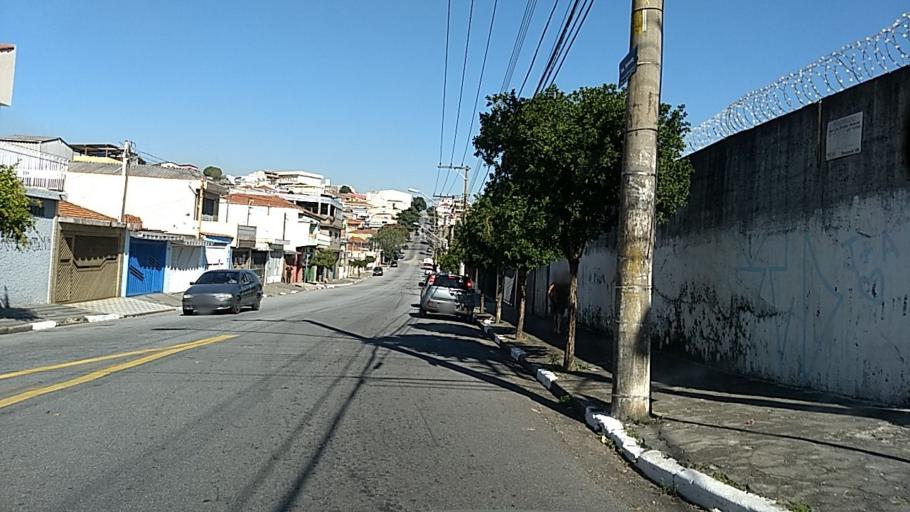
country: BR
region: Sao Paulo
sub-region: Guarulhos
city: Guarulhos
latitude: -23.4920
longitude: -46.5816
